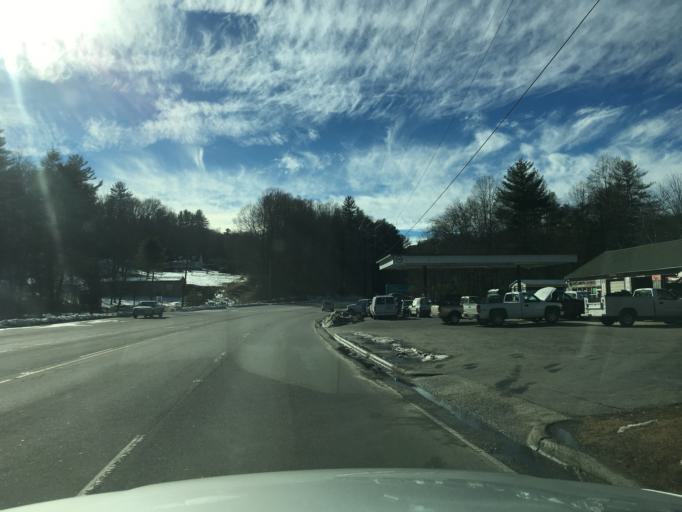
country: US
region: North Carolina
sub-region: Transylvania County
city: Brevard
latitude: 35.2223
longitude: -82.7437
